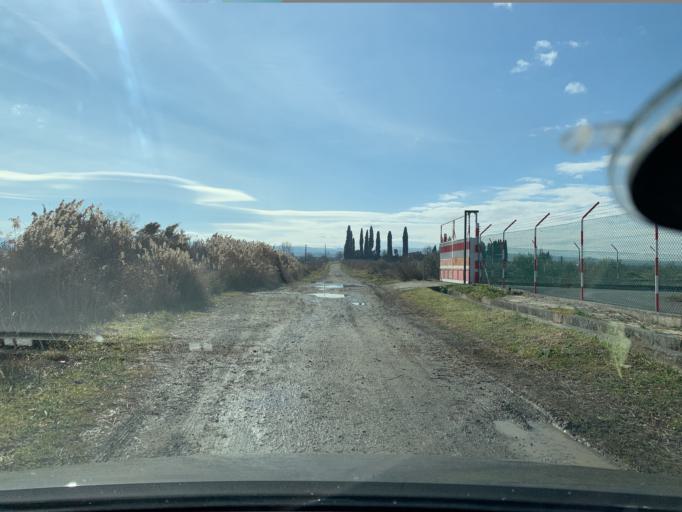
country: ES
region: Andalusia
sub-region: Provincia de Granada
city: Chauchina
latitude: 37.1884
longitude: -3.7580
